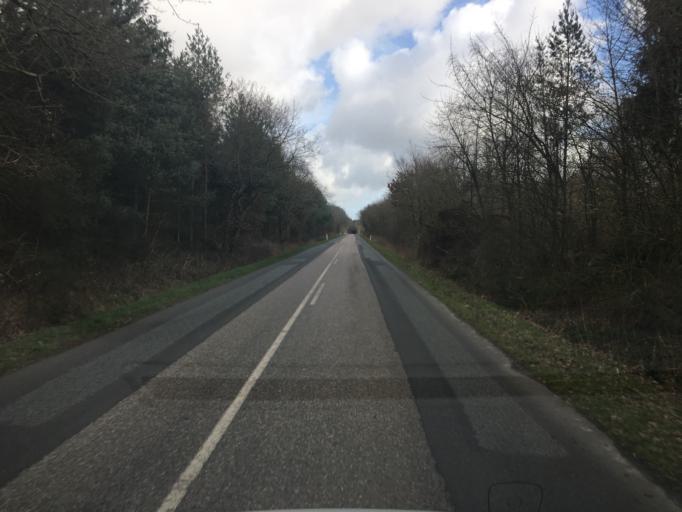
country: DK
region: South Denmark
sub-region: Aabenraa Kommune
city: Krusa
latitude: 54.8993
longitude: 9.4585
